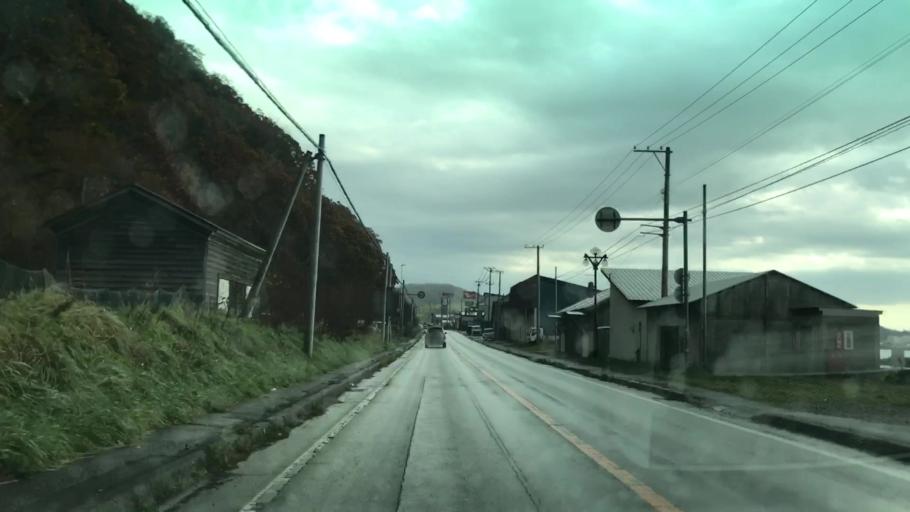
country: JP
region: Hokkaido
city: Shizunai-furukawacho
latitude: 42.1771
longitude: 142.7508
